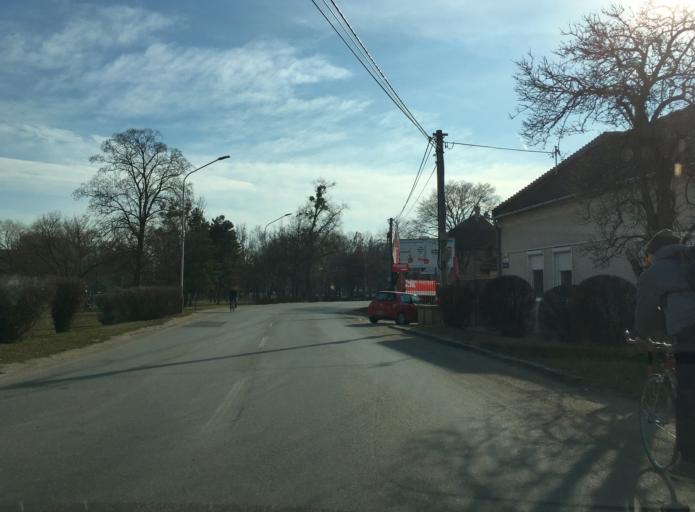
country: SK
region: Nitriansky
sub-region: Okres Nove Zamky
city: Nove Zamky
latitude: 47.9902
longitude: 18.1582
